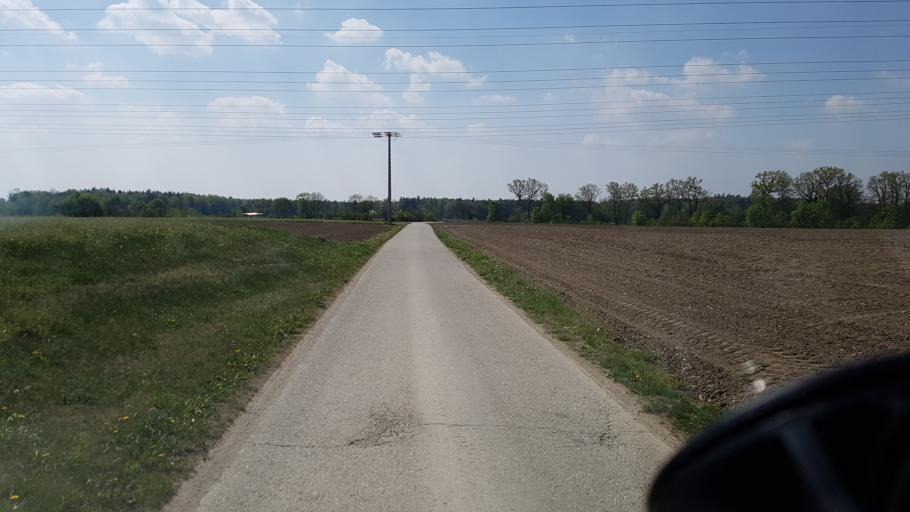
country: DE
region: Bavaria
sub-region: Upper Bavaria
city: Perach
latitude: 48.2526
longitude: 12.8023
